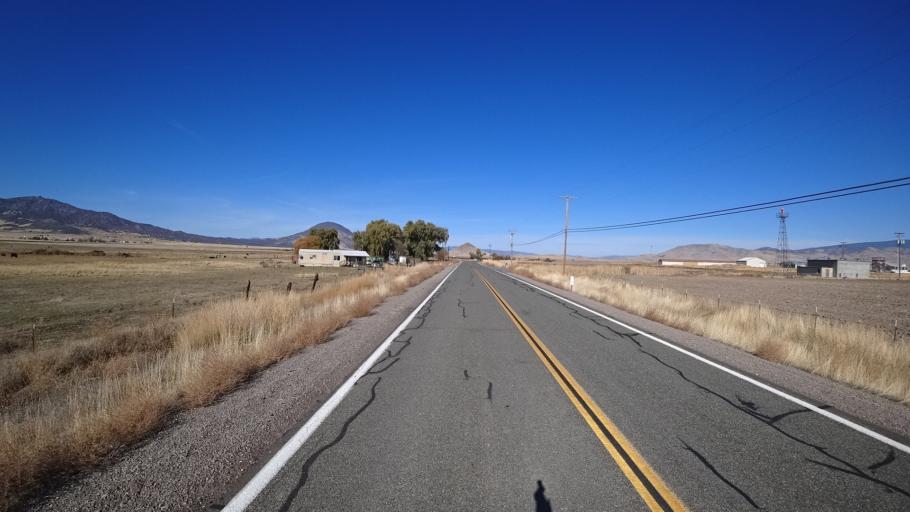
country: US
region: California
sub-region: Siskiyou County
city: Montague
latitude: 41.7802
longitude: -122.4737
